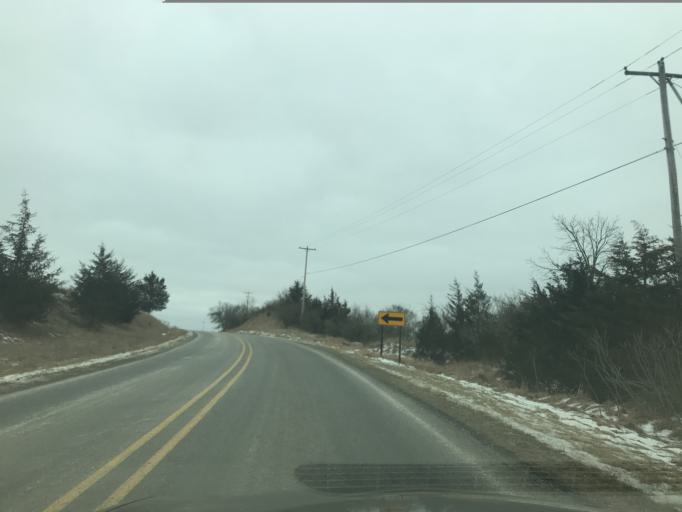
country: US
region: Michigan
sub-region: Jackson County
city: Brooklyn
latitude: 42.0581
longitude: -84.3257
